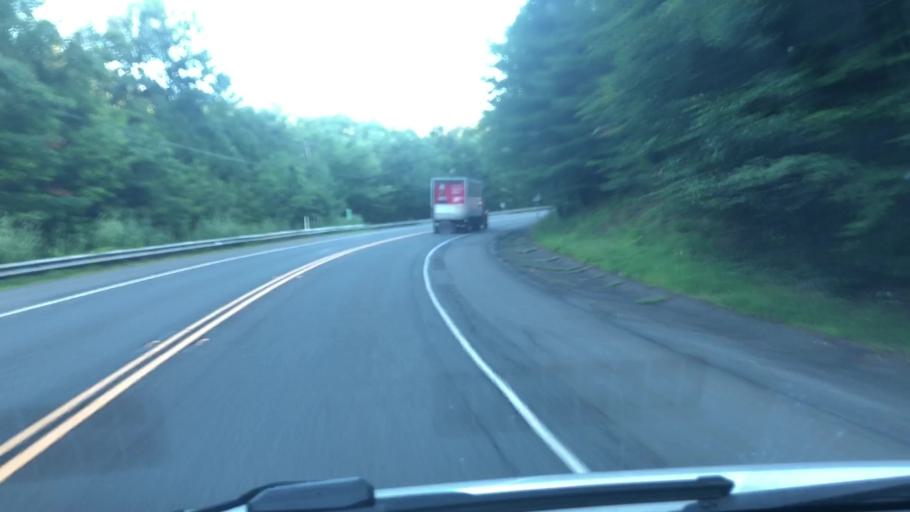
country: US
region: Massachusetts
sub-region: Hampshire County
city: Chesterfield
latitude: 42.4406
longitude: -72.8680
